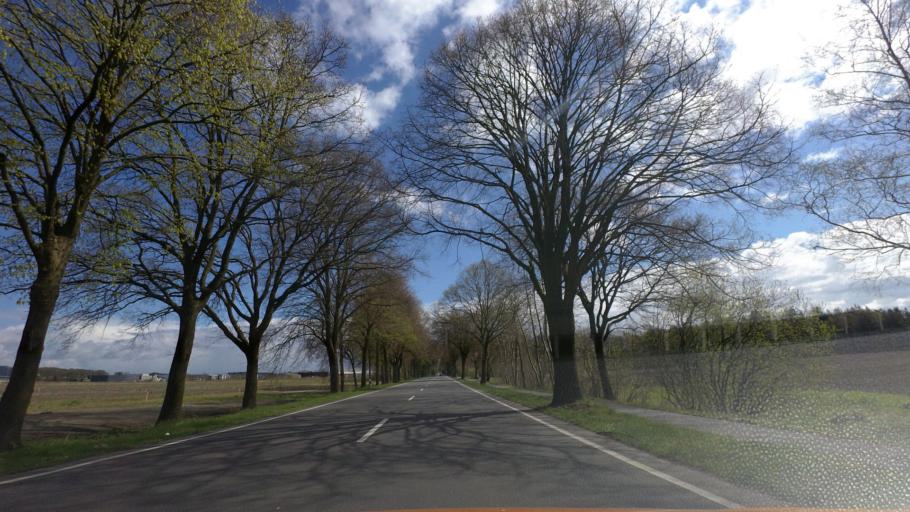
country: DE
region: Lower Saxony
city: Botersen
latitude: 53.1220
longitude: 9.3413
